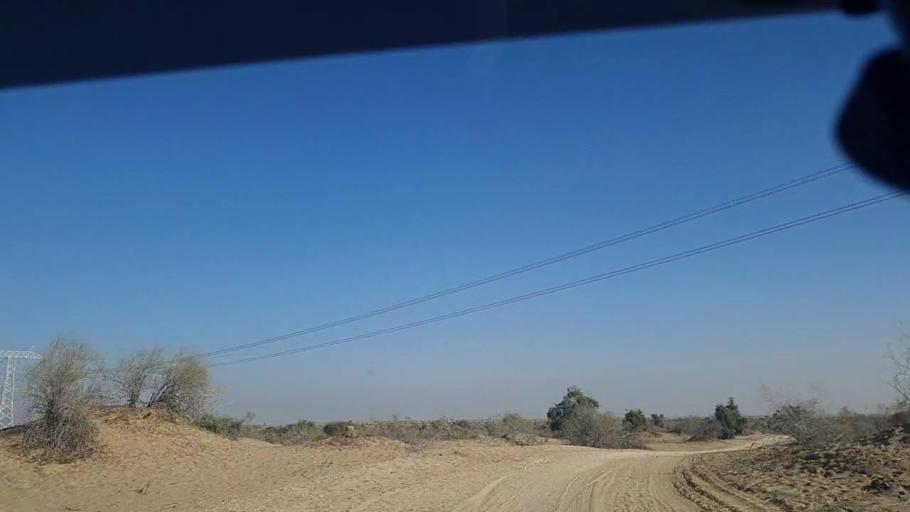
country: PK
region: Sindh
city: Khanpur
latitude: 27.6449
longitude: 69.4047
